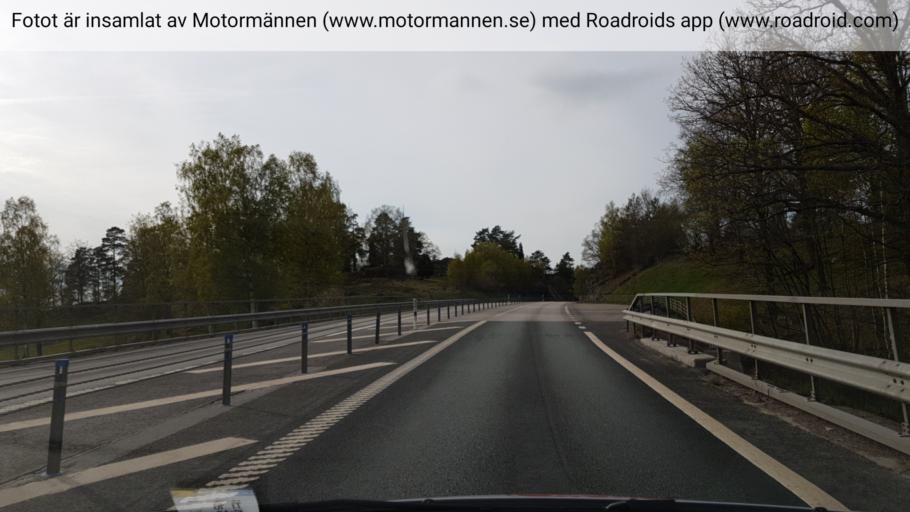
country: SE
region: Kalmar
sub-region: Vasterviks Kommun
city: Gamleby
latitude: 57.8826
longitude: 16.3910
